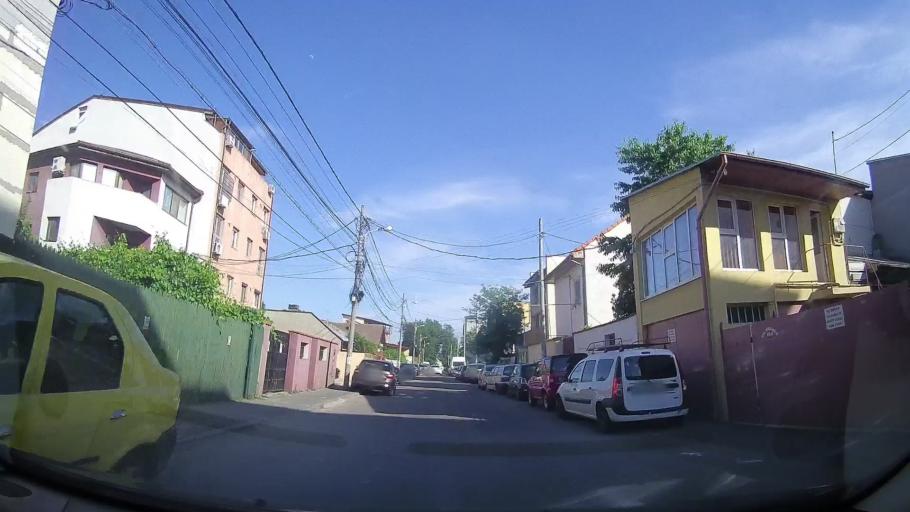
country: RO
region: Bucuresti
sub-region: Municipiul Bucuresti
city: Bucharest
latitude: 44.4106
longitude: 26.1320
